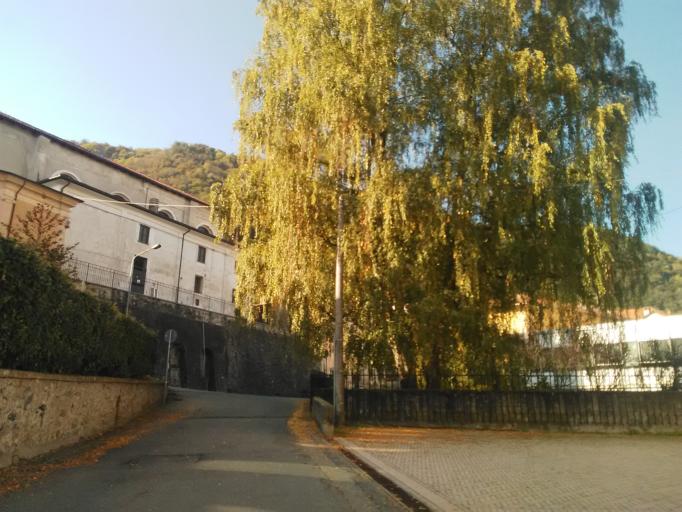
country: IT
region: Piedmont
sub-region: Provincia di Vercelli
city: Borgosesia
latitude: 45.7099
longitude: 8.2771
